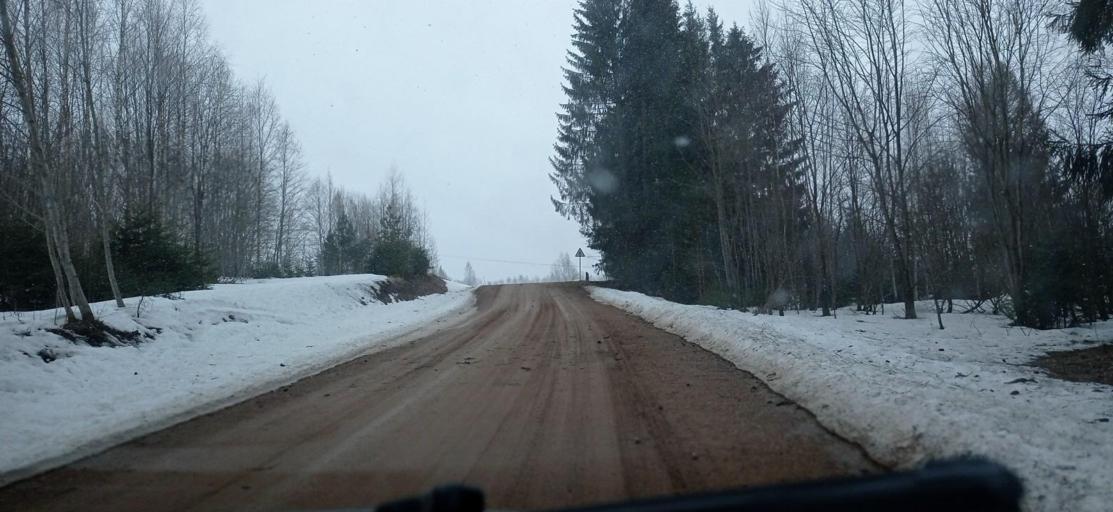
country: EE
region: Tartu
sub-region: UElenurme vald
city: Ulenurme
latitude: 58.1146
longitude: 26.6995
